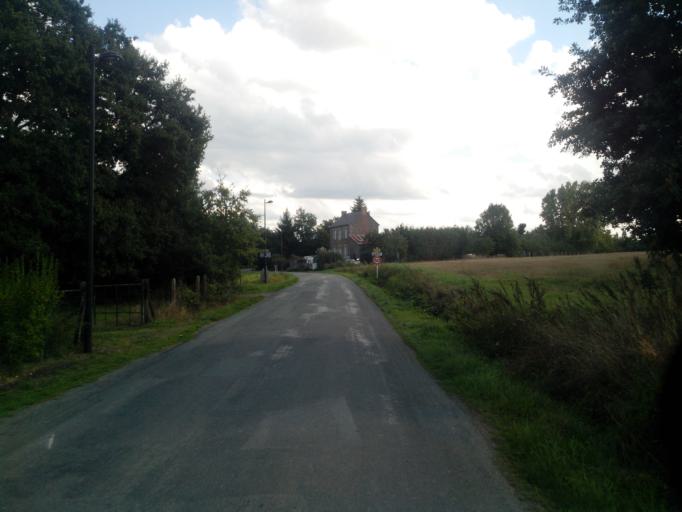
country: FR
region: Brittany
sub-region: Departement d'Ille-et-Vilaine
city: Gael
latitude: 48.1266
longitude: -2.1537
